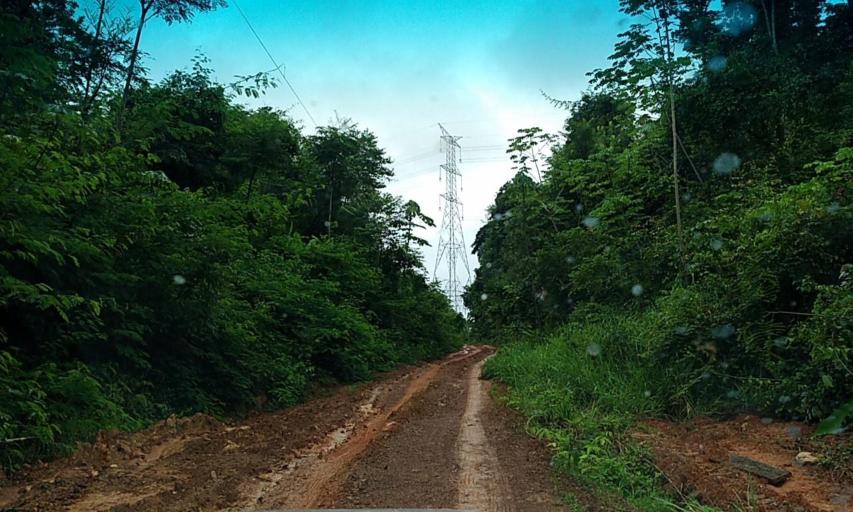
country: BR
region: Para
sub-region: Altamira
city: Altamira
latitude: -3.1131
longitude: -51.6028
